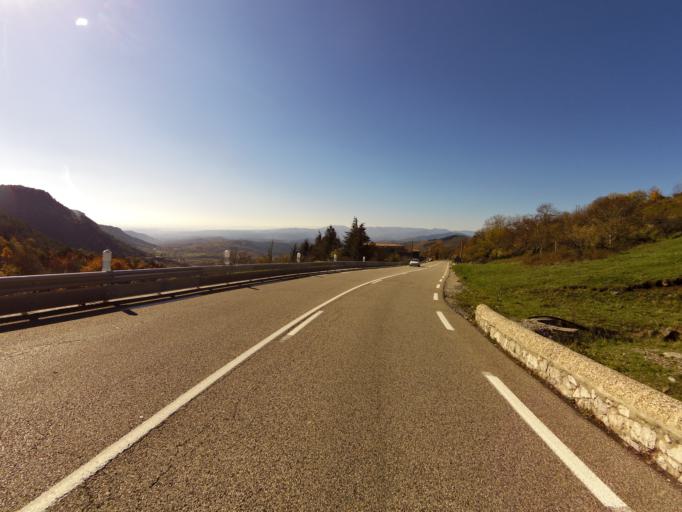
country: FR
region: Rhone-Alpes
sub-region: Departement de l'Ardeche
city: Saint-Priest
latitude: 44.7174
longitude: 4.4927
